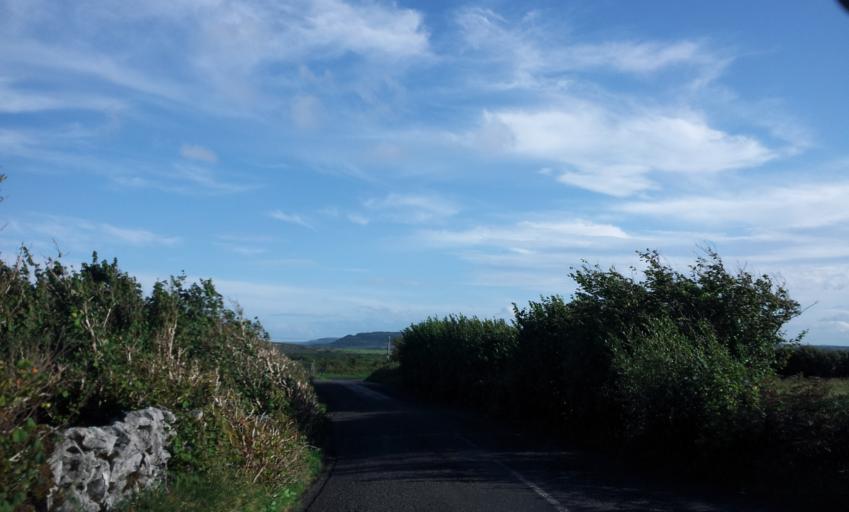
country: IE
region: Munster
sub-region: An Clar
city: Ennis
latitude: 53.0077
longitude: -9.1280
